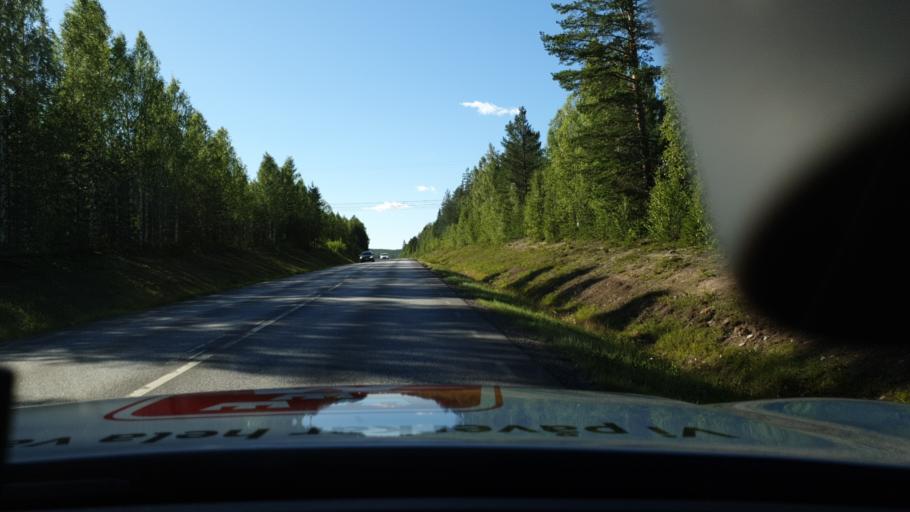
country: SE
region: Norrbotten
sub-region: Pitea Kommun
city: Norrfjarden
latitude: 65.6144
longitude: 21.4395
